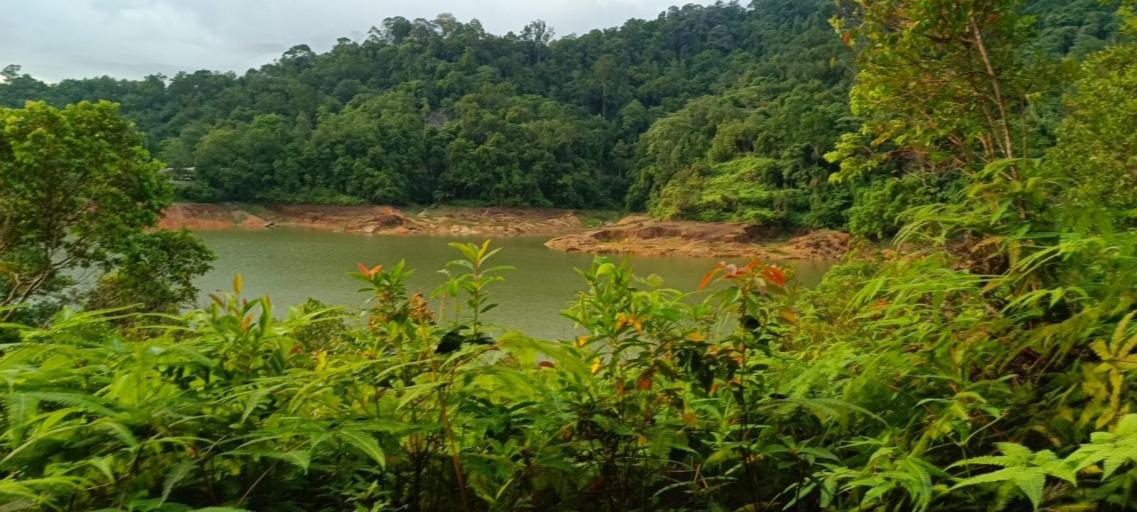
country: MY
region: Penang
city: Kampung Sungai Ara
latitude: 5.3961
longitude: 100.2603
